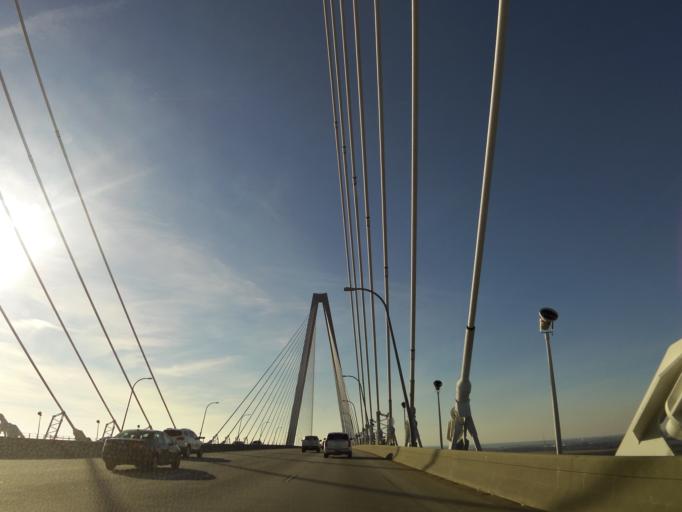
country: US
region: South Carolina
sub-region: Charleston County
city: Charleston
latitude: 32.8028
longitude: -79.9137
